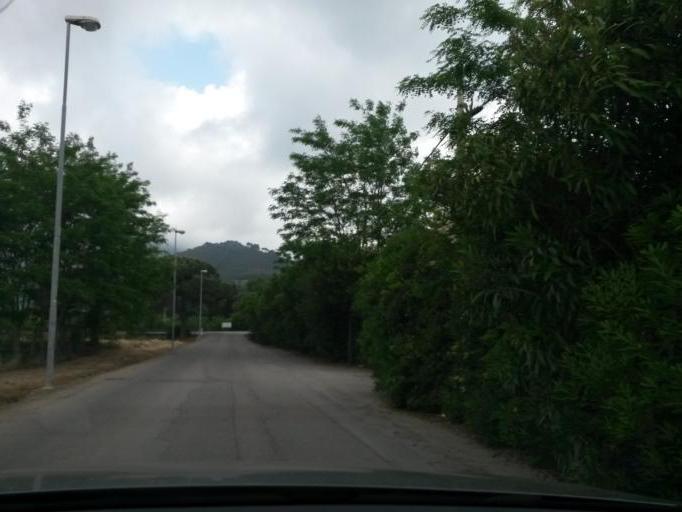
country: IT
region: Tuscany
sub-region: Provincia di Livorno
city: Porto Azzurro
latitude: 42.7728
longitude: 10.4048
